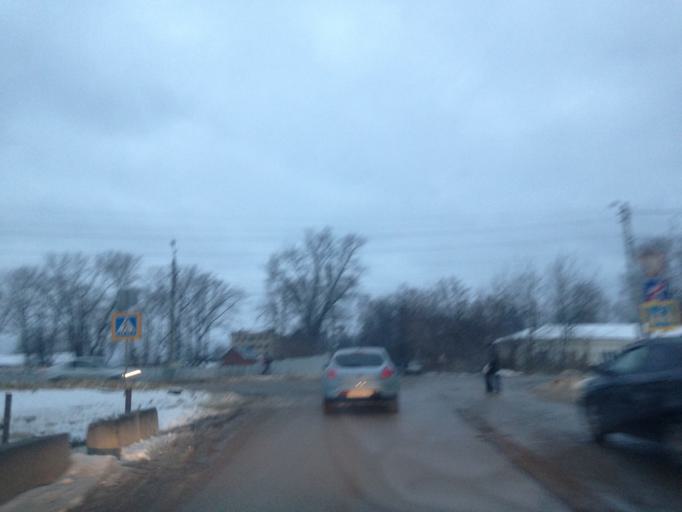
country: RU
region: Tula
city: Shchekino
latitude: 53.9989
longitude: 37.5102
